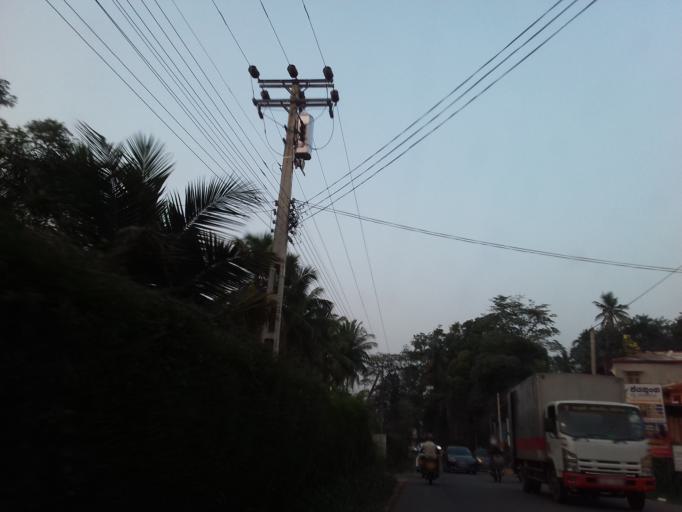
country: LK
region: Western
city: Welisara
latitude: 7.0415
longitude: 79.9574
